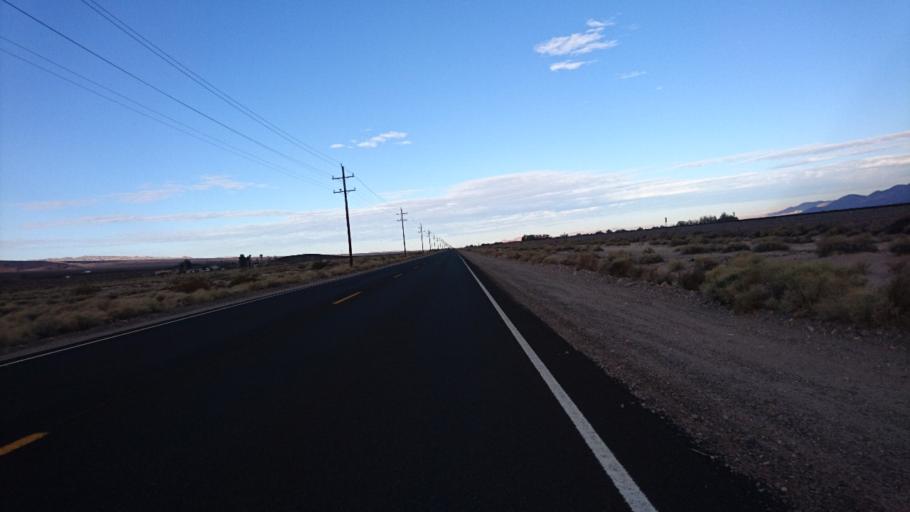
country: US
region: California
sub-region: San Bernardino County
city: Barstow
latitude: 34.8367
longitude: -116.7173
